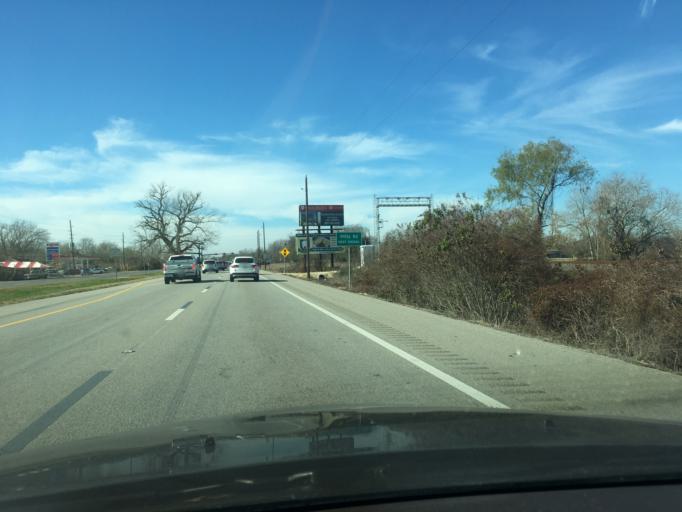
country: US
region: Texas
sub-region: Fort Bend County
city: Pecan Grove
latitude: 29.5969
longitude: -95.7312
